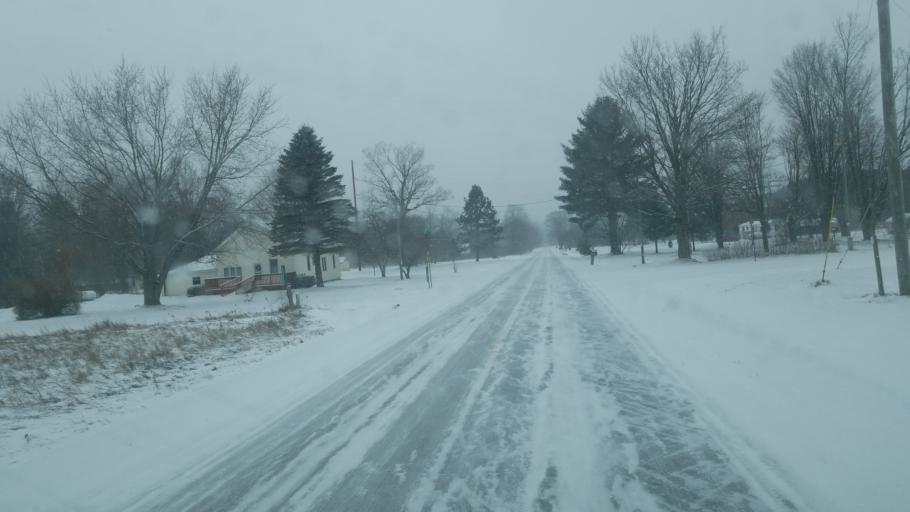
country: US
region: Michigan
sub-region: Osceola County
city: Reed City
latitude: 43.8218
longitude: -85.4135
